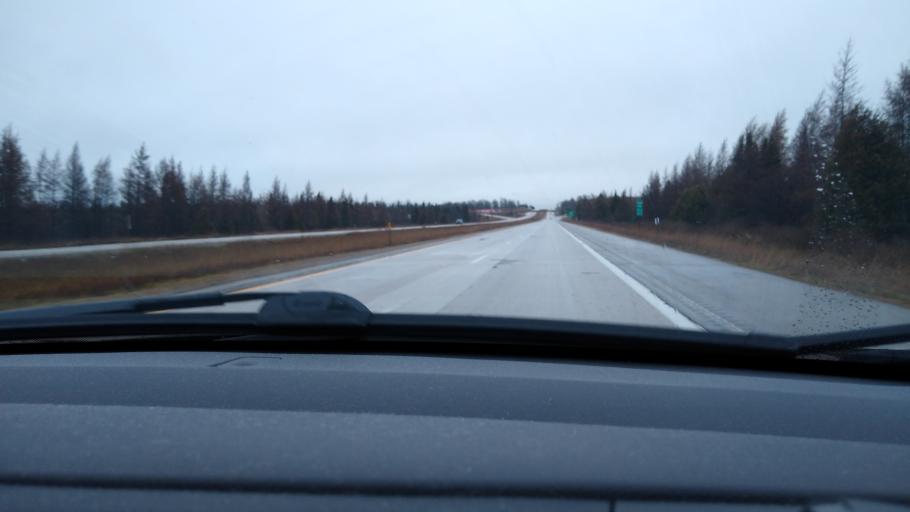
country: US
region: Michigan
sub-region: Cheboygan County
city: Cheboygan
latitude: 45.6454
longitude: -84.6350
